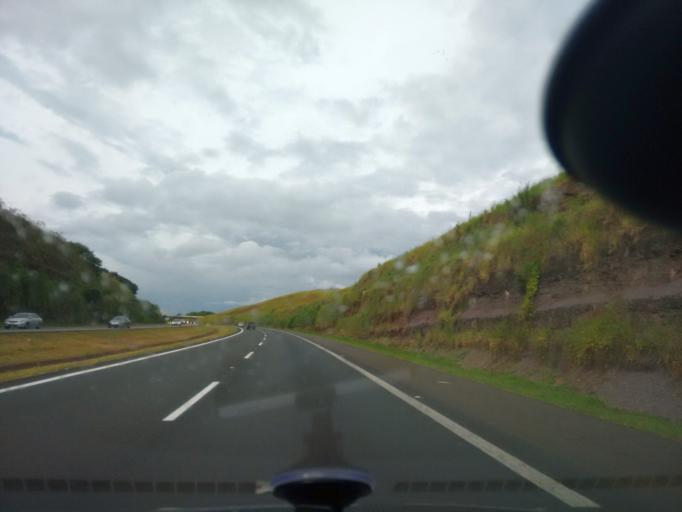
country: BR
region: Sao Paulo
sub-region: Cordeiropolis
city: Cordeiropolis
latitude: -22.5390
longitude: -47.4533
